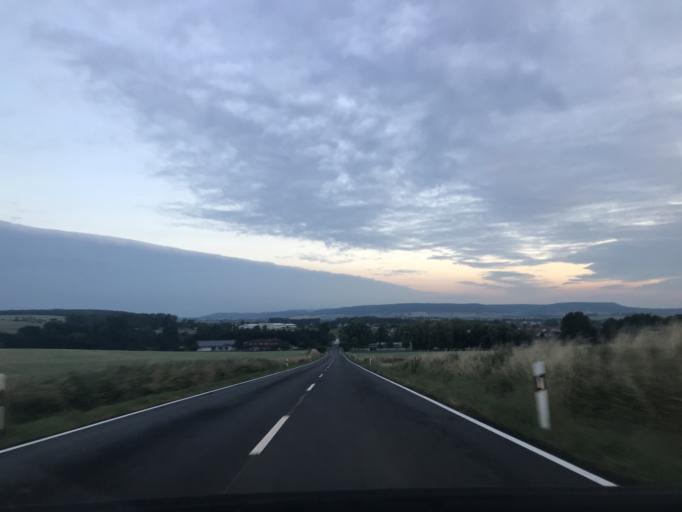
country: DE
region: Thuringia
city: Niederorschel
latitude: 51.3592
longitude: 10.4262
